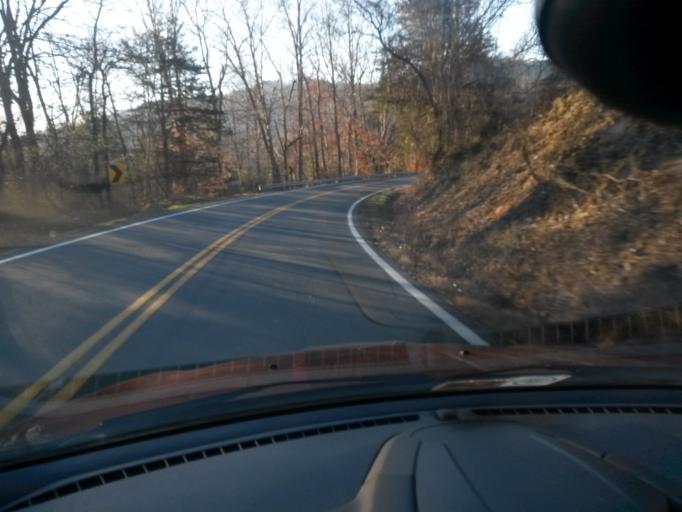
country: US
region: Virginia
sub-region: City of Buena Vista
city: Buena Vista
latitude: 37.6954
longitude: -79.2428
